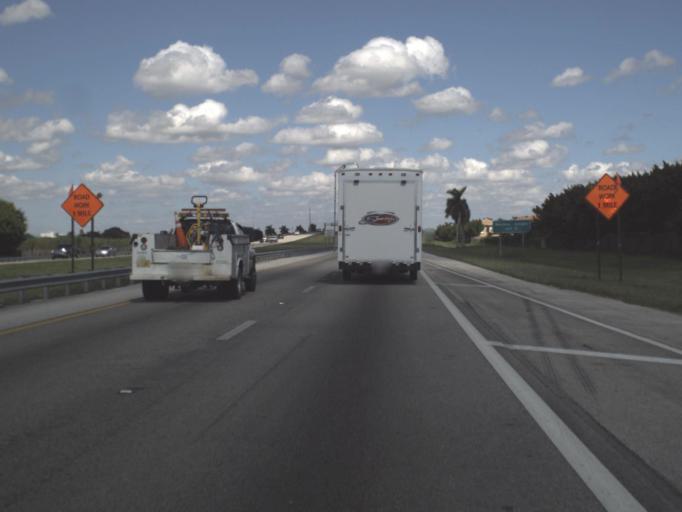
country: US
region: Florida
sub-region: Miami-Dade County
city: Goulds
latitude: 25.5540
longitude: -80.3627
